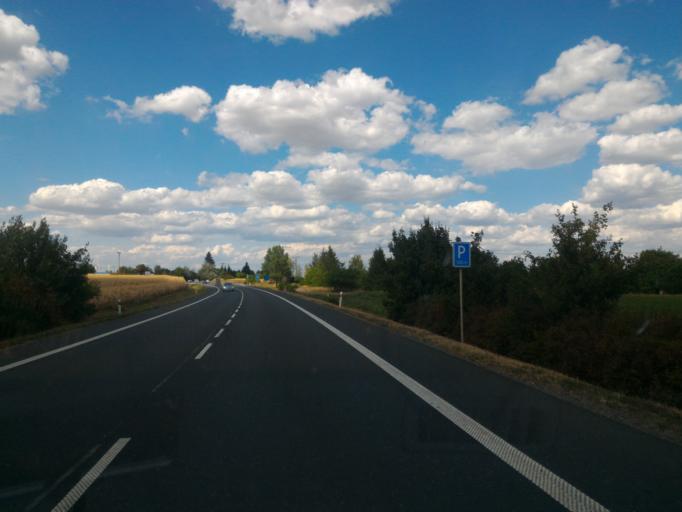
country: CZ
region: Central Bohemia
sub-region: Okres Kutna Hora
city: Caslav
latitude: 49.9177
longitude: 15.4030
